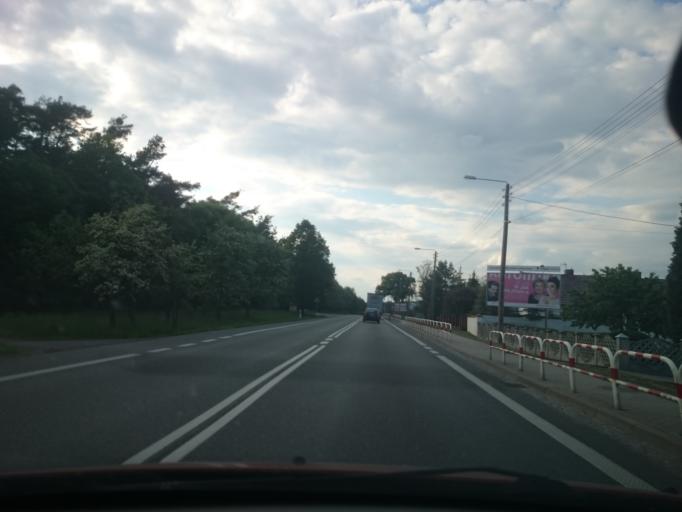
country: PL
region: Opole Voivodeship
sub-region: Powiat opolski
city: Tarnow Opolski
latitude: 50.6059
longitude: 18.0742
